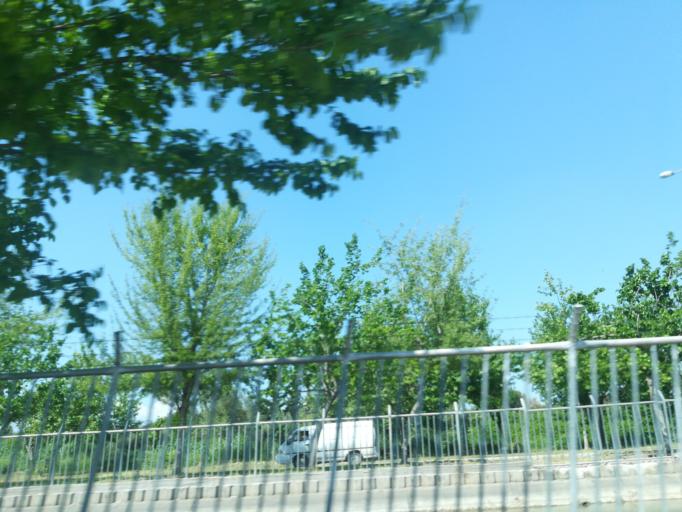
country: TR
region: Adana
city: Adana
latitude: 37.0245
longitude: 35.3658
